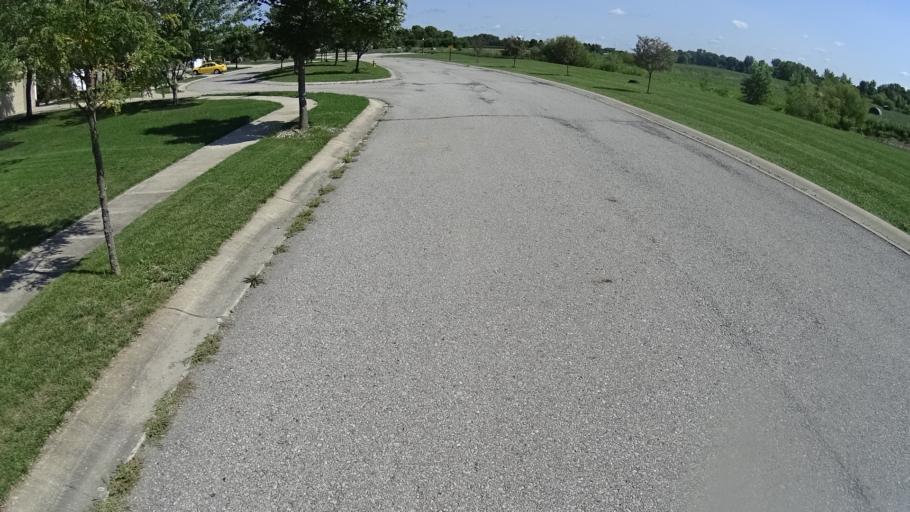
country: US
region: Indiana
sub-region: Madison County
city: Pendleton
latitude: 39.9826
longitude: -85.7440
